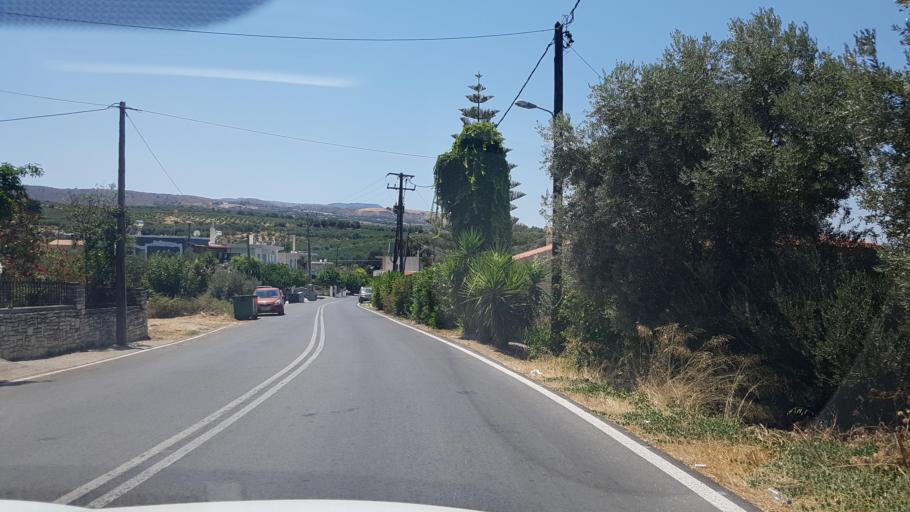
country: GR
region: Crete
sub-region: Nomos Rethymnis
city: Rethymno
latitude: 35.3566
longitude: 24.5870
